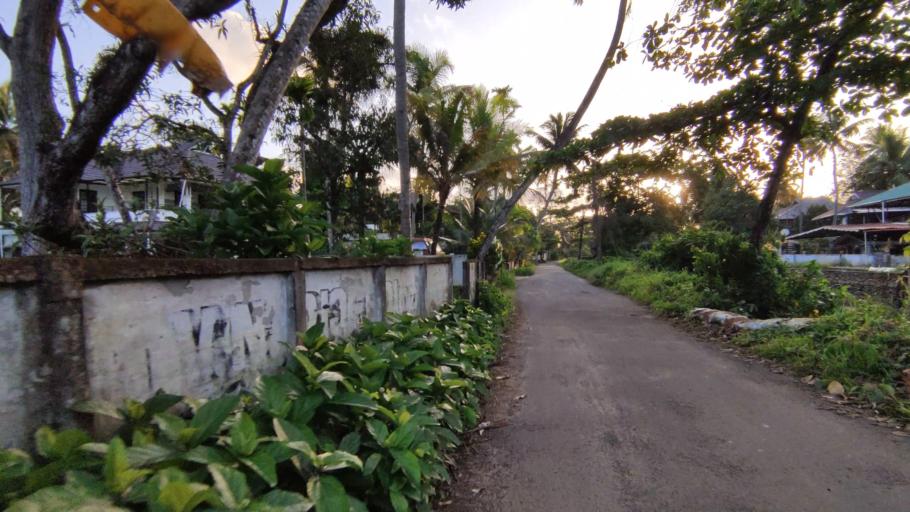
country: IN
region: Kerala
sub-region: Kottayam
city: Kottayam
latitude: 9.5958
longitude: 76.4650
